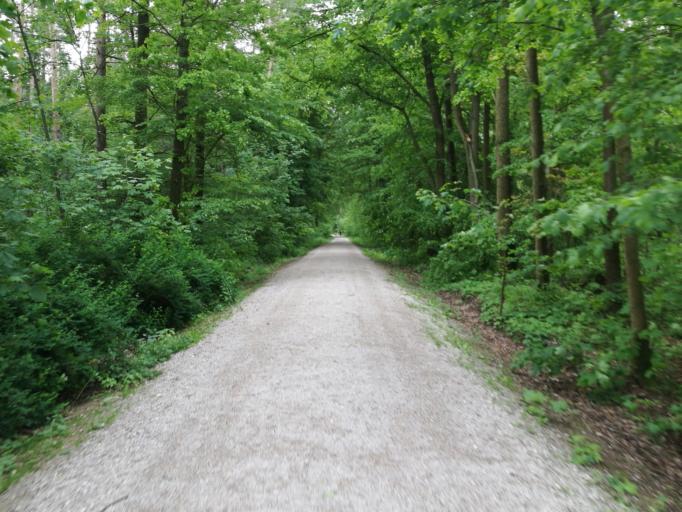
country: DE
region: Bavaria
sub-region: Regierungsbezirk Mittelfranken
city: Seukendorf
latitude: 49.4665
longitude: 10.8895
